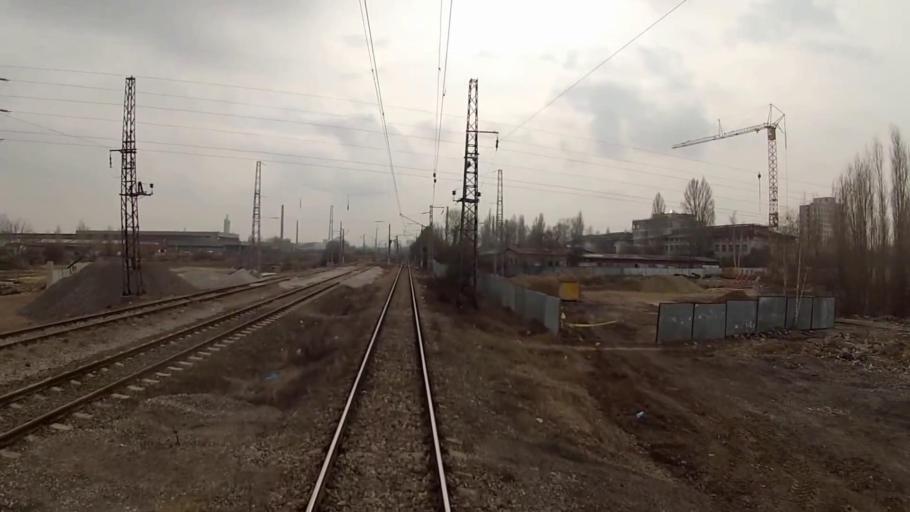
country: BG
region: Sofia-Capital
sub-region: Stolichna Obshtina
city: Sofia
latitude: 42.6625
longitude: 23.4228
